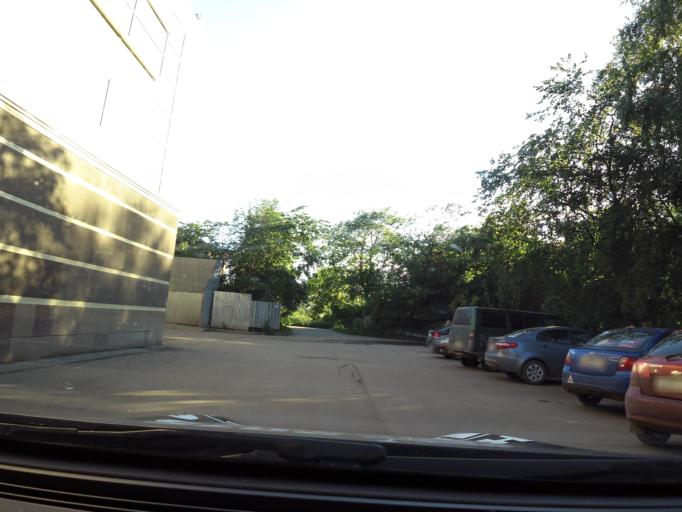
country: RU
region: Vologda
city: Vologda
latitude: 59.2218
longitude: 39.9121
